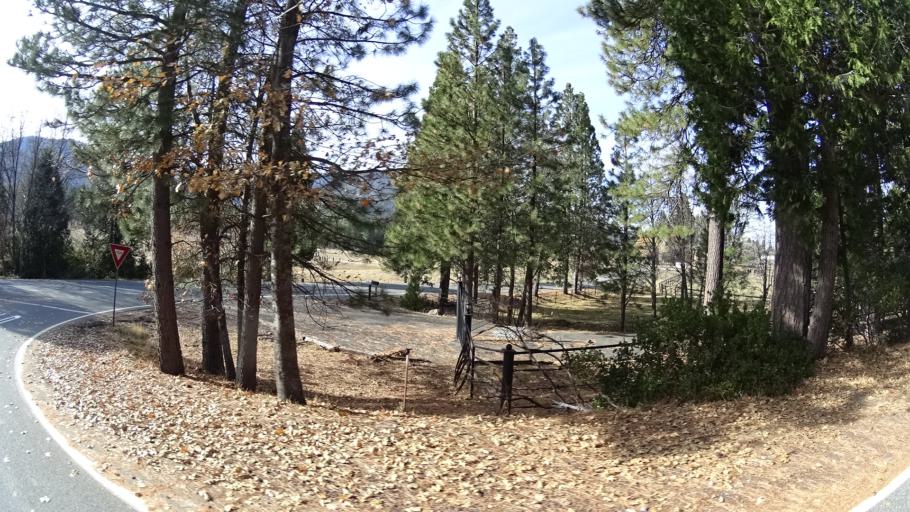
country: US
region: California
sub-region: Siskiyou County
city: Weed
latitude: 41.4000
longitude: -122.4202
